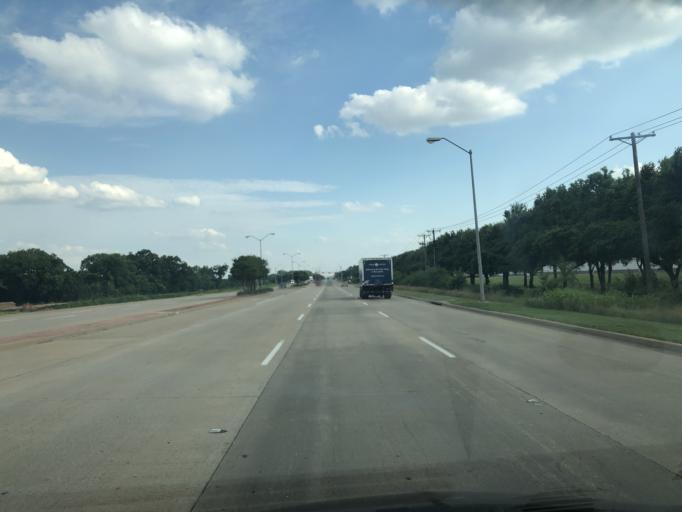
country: US
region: Texas
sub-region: Dallas County
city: Irving
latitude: 32.8013
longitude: -96.9946
